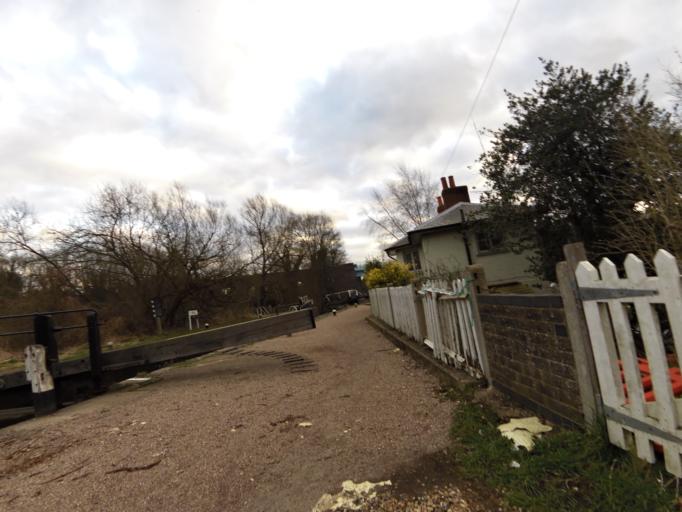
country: GB
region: England
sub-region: Hertfordshire
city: Watford
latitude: 51.6546
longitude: -0.4278
